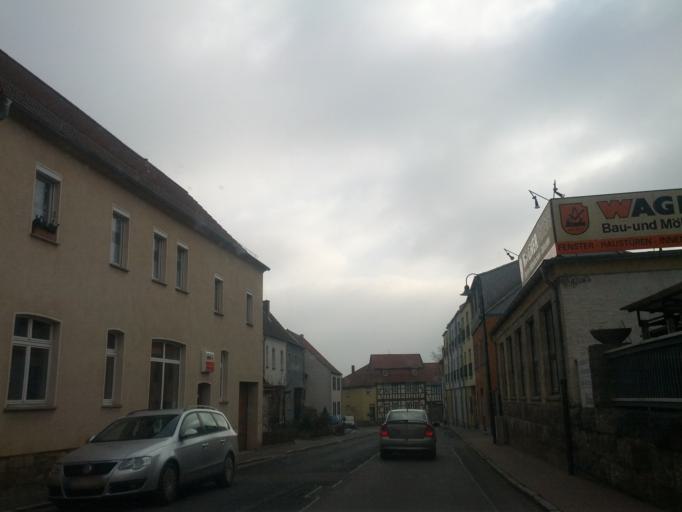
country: DE
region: Thuringia
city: Creuzburg
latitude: 51.0517
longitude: 10.2478
